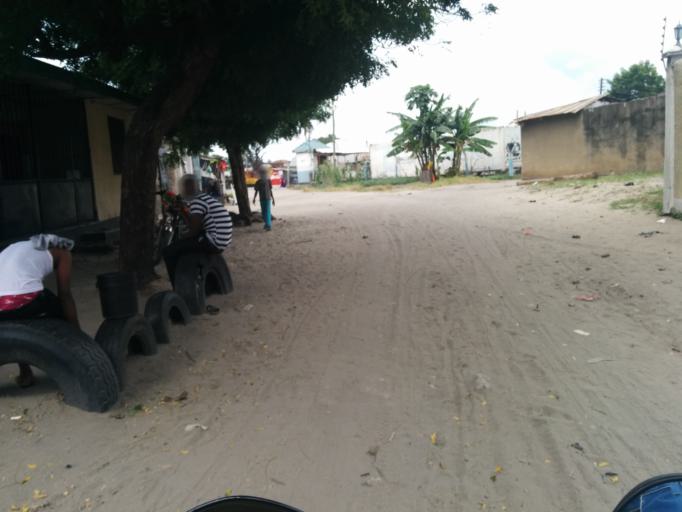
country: TZ
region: Dar es Salaam
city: Dar es Salaam
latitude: -6.8622
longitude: 39.2546
